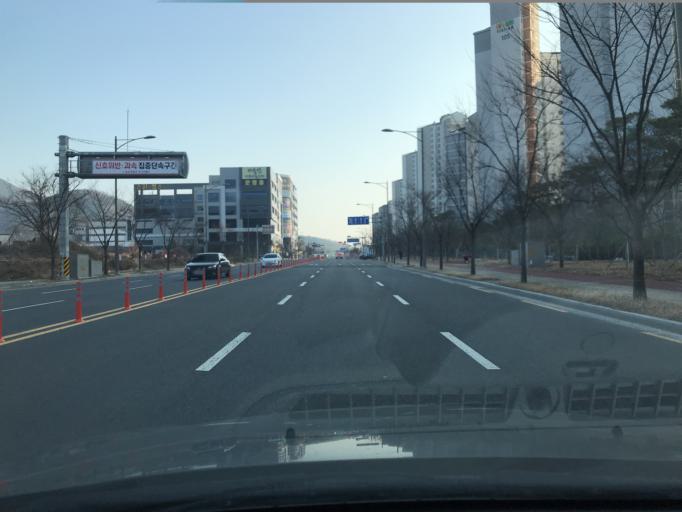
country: KR
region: Daegu
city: Hwawon
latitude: 35.6960
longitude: 128.4698
